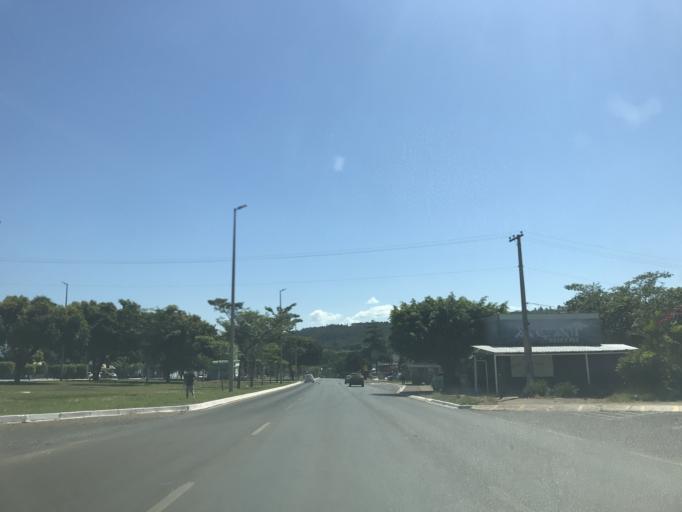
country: BR
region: Federal District
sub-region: Brasilia
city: Brasilia
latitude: -15.6465
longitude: -47.7864
